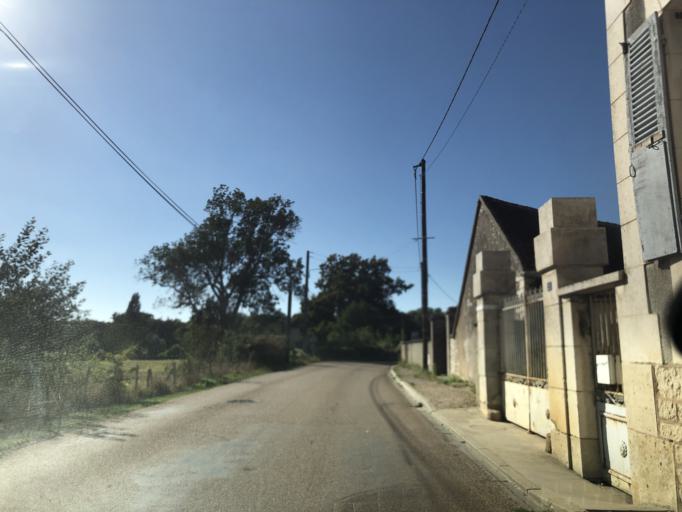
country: FR
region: Bourgogne
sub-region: Departement de l'Yonne
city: Cheny
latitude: 47.9238
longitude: 3.5259
